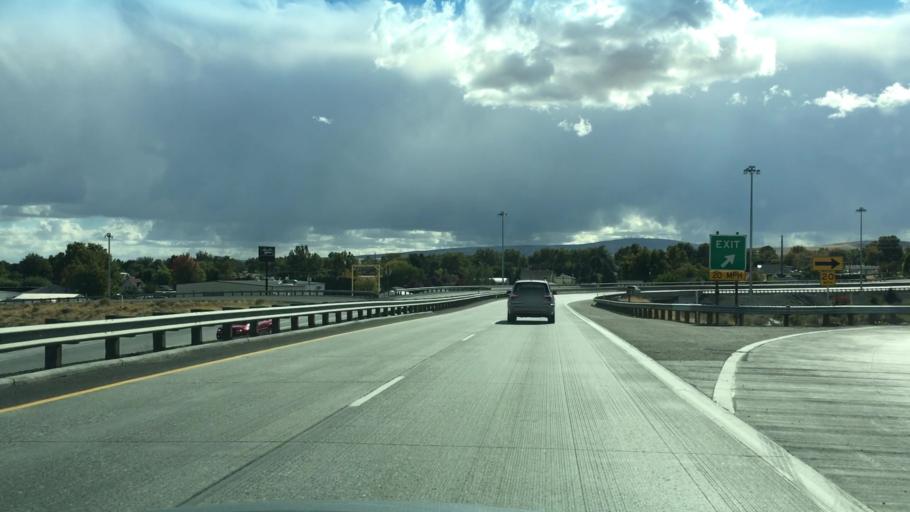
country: US
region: Washington
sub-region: Benton County
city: Kennewick
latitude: 46.2184
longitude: -119.1382
